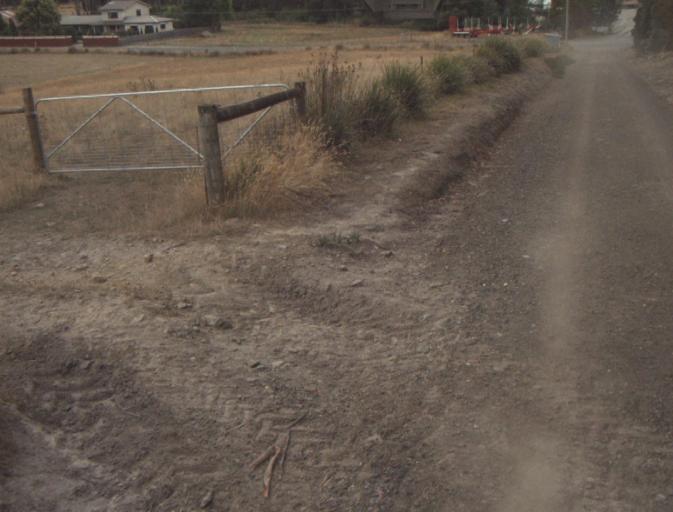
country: AU
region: Tasmania
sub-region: Launceston
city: Mayfield
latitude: -41.2388
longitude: 147.1863
